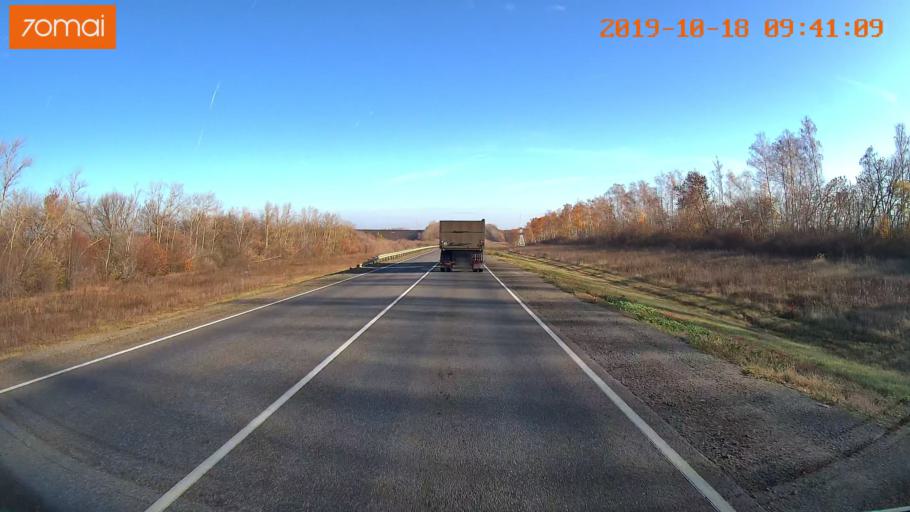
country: RU
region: Tula
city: Kazachka
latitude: 53.2718
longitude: 38.1579
